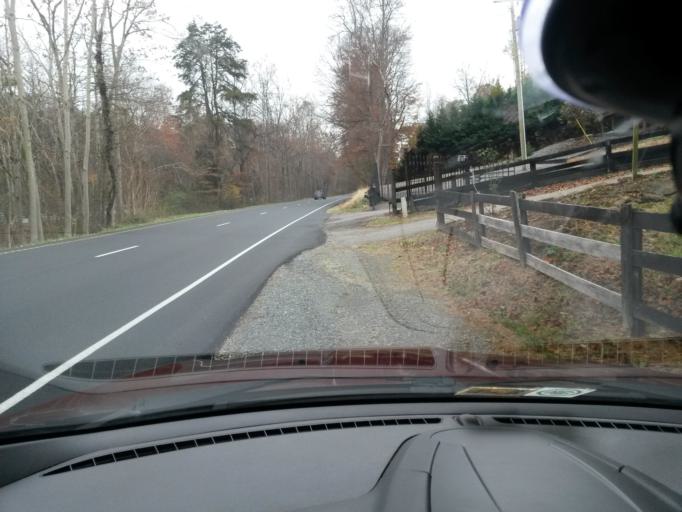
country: US
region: Virginia
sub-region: Albemarle County
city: Crozet
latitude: 37.9483
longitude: -78.6636
